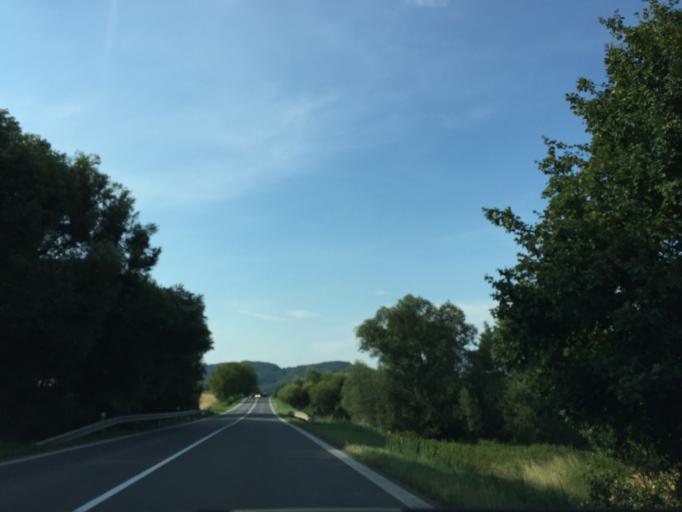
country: SK
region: Presovsky
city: Giraltovce
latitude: 49.0140
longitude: 21.5353
